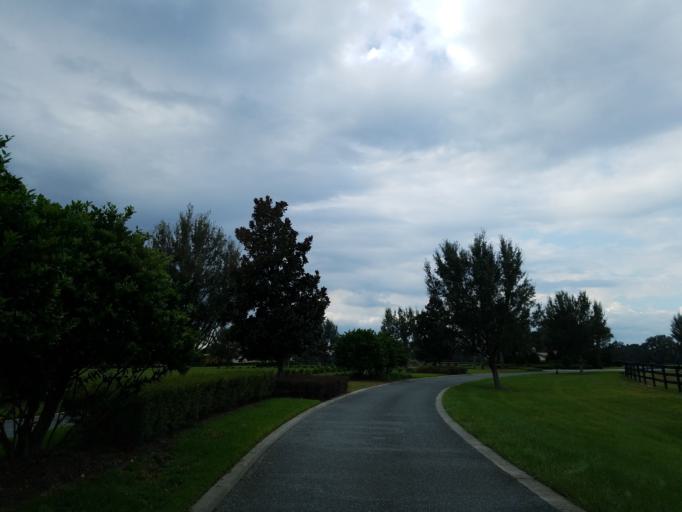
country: US
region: Florida
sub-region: Citrus County
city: Hernando
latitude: 29.0170
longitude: -82.3228
